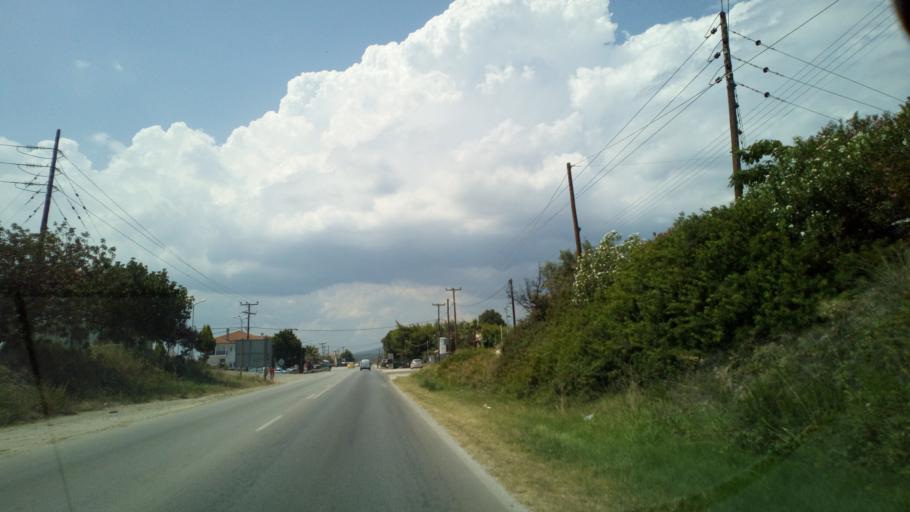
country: GR
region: Central Macedonia
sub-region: Nomos Chalkidikis
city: Nikiti
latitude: 40.2174
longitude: 23.6768
